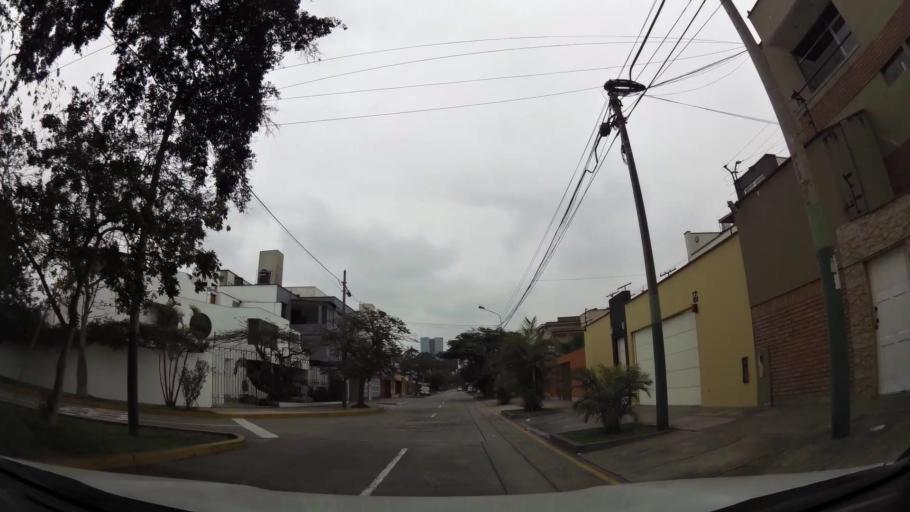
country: PE
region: Lima
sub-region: Lima
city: San Luis
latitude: -12.0976
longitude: -77.0000
